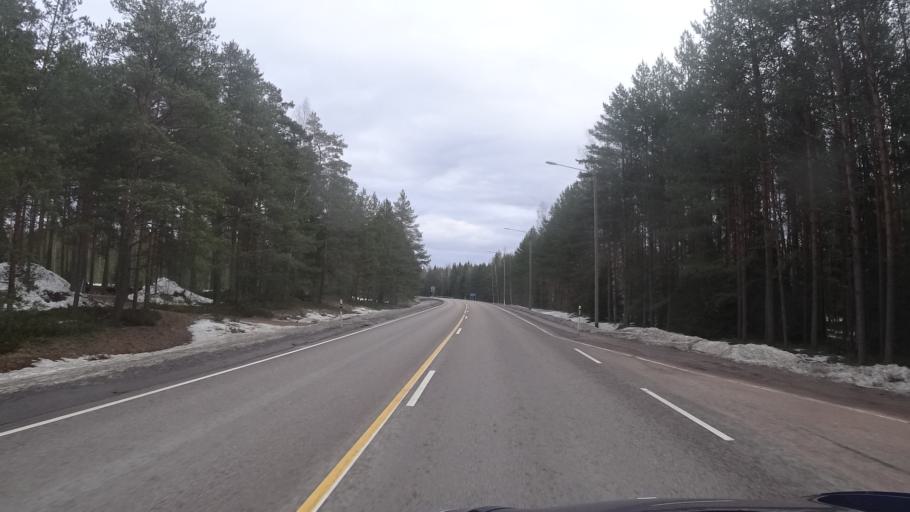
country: FI
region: Kymenlaakso
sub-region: Kouvola
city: Anjala
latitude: 60.6923
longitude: 26.7018
